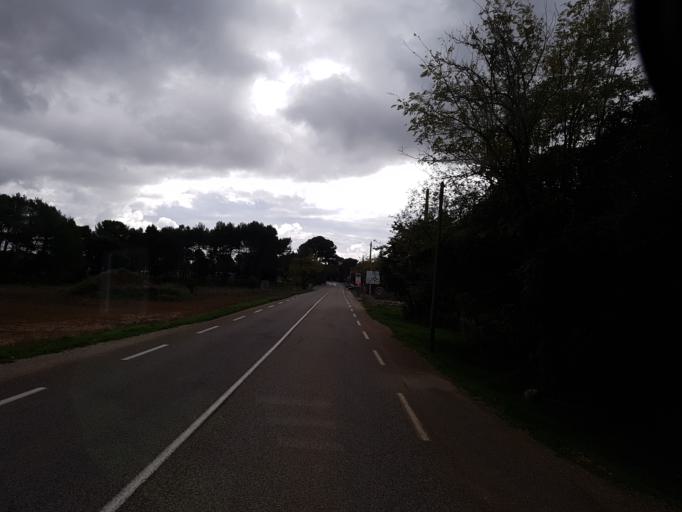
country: FR
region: Provence-Alpes-Cote d'Azur
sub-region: Departement des Bouches-du-Rhone
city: Cuges-les-Pins
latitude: 43.2596
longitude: 5.7496
